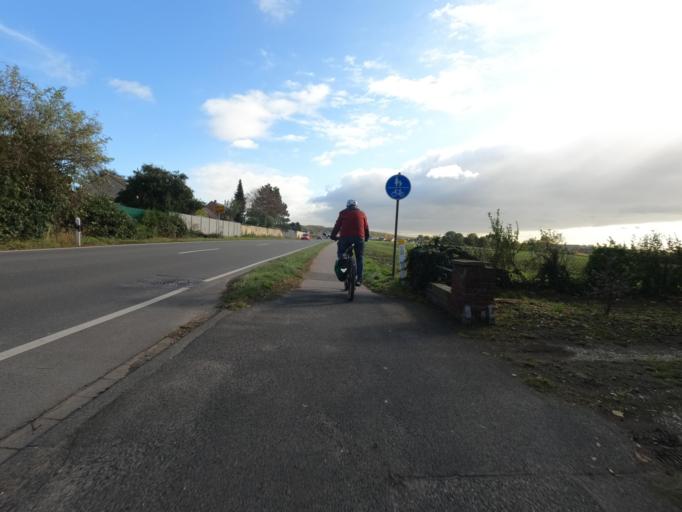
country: DE
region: North Rhine-Westphalia
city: Huckelhoven
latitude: 51.0476
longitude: 6.2317
